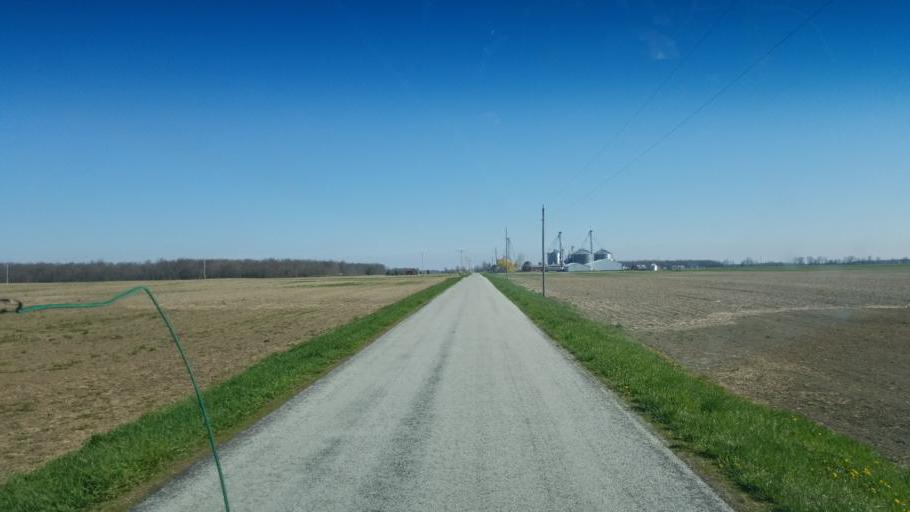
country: US
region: Ohio
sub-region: Hardin County
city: Kenton
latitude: 40.6706
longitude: -83.5621
